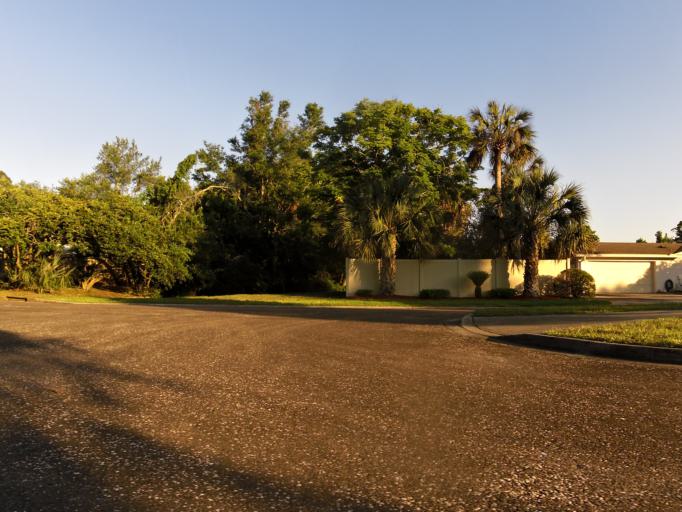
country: US
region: Florida
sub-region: Duval County
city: Jacksonville
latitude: 30.2323
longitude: -81.6161
